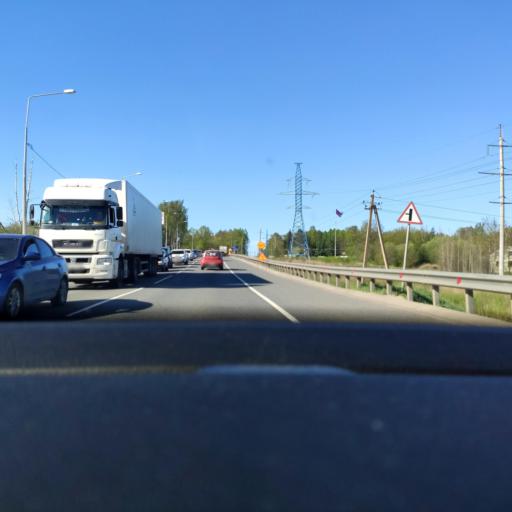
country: RU
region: Moskovskaya
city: Dmitrov
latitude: 56.3552
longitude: 37.4874
